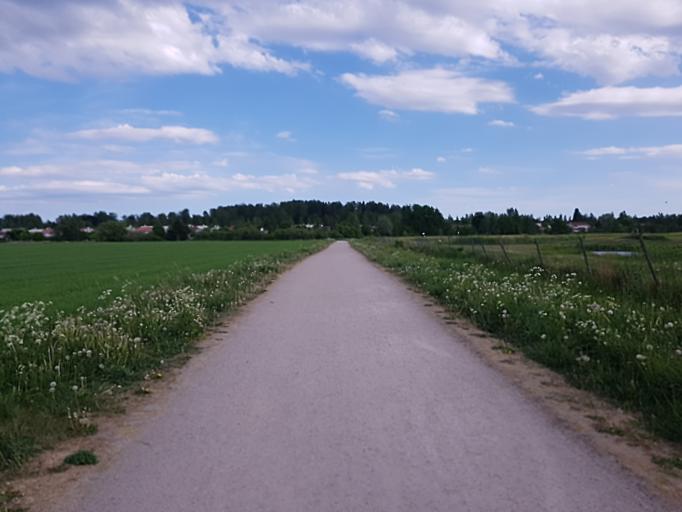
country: FI
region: Uusimaa
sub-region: Helsinki
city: Helsinki
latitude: 60.2654
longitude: 24.9434
